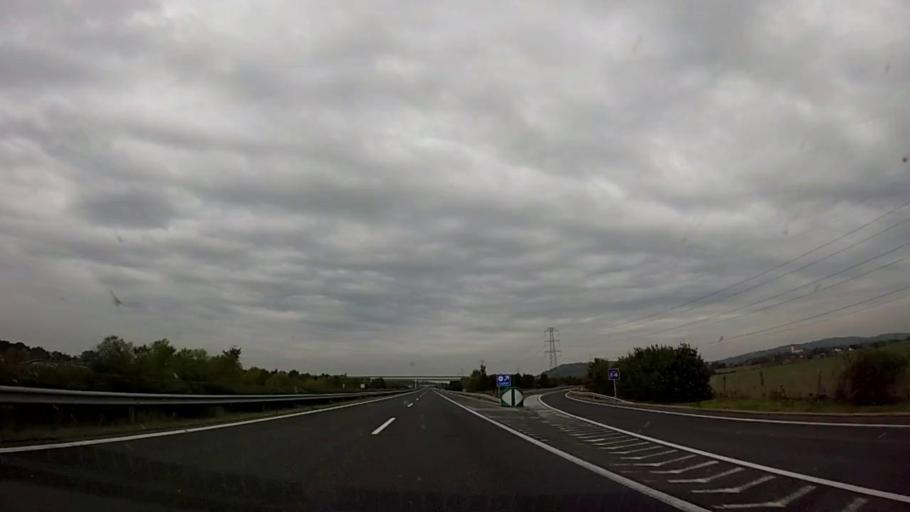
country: HR
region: Medimurska
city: Podturen
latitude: 46.5093
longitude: 16.5648
